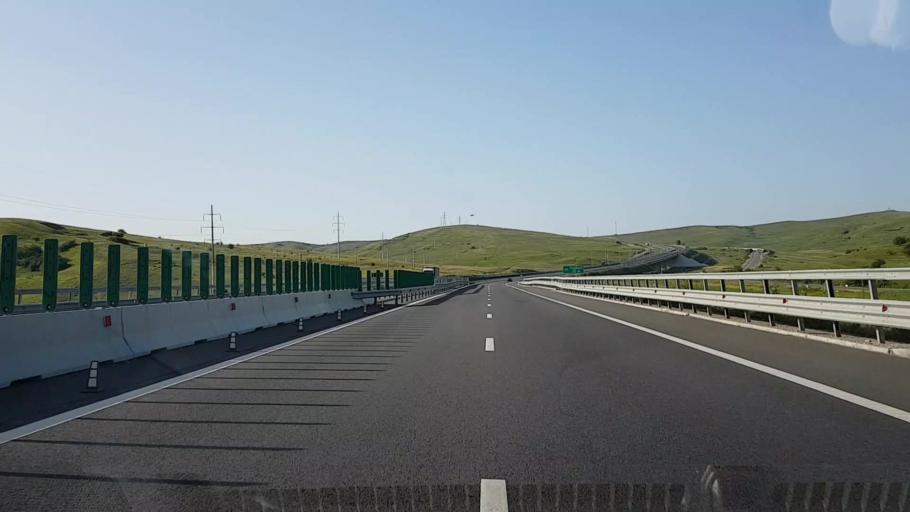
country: RO
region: Cluj
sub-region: Comuna Mihai Viteazu
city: Mihai Viteazu
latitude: 46.4821
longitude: 23.7763
